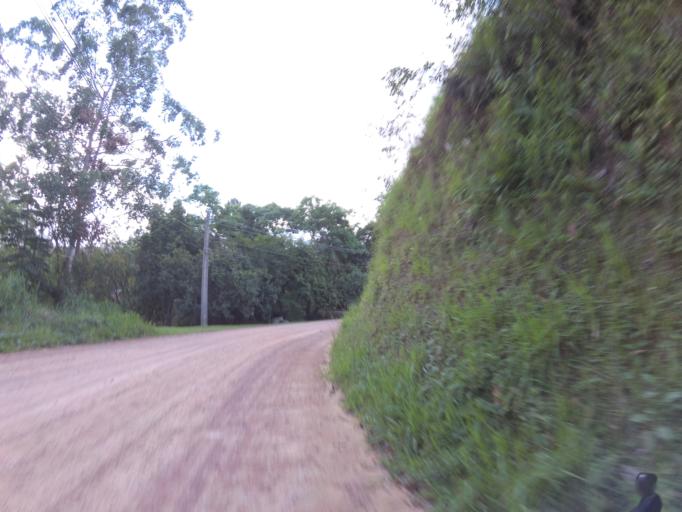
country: BR
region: Santa Catarina
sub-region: Pomerode
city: Pomerode
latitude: -26.8022
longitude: -49.1592
